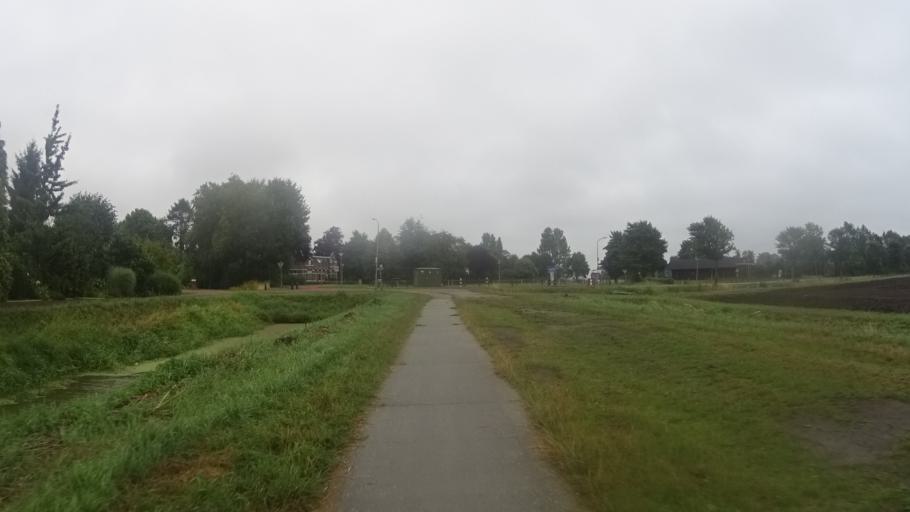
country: NL
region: Groningen
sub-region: Gemeente Slochteren
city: Slochteren
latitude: 53.1921
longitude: 6.8791
